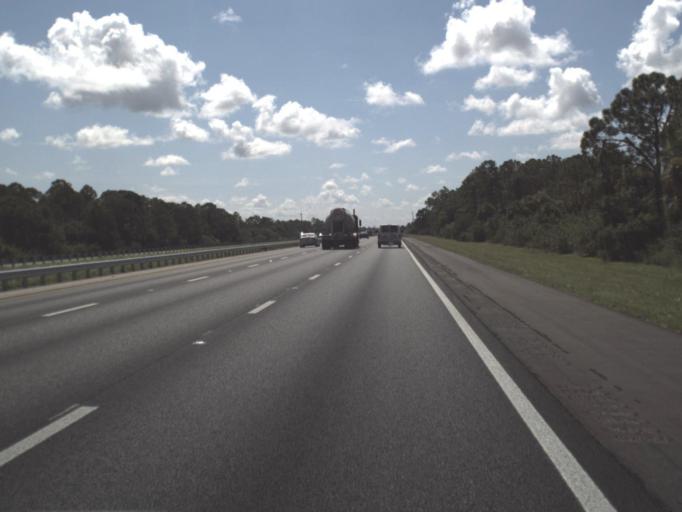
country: US
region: Florida
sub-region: Lee County
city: Suncoast Estates
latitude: 26.7365
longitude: -81.8472
